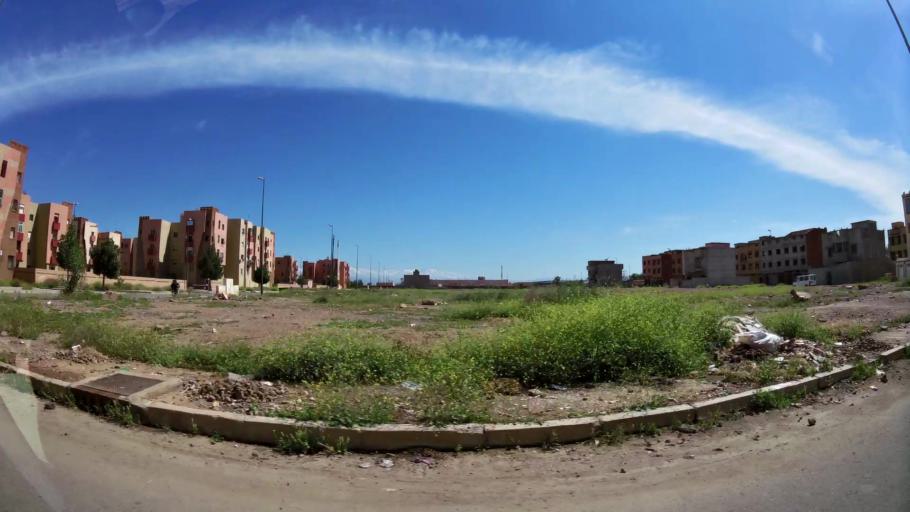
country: MA
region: Marrakech-Tensift-Al Haouz
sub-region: Marrakech
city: Marrakesh
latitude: 31.6365
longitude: -8.0808
